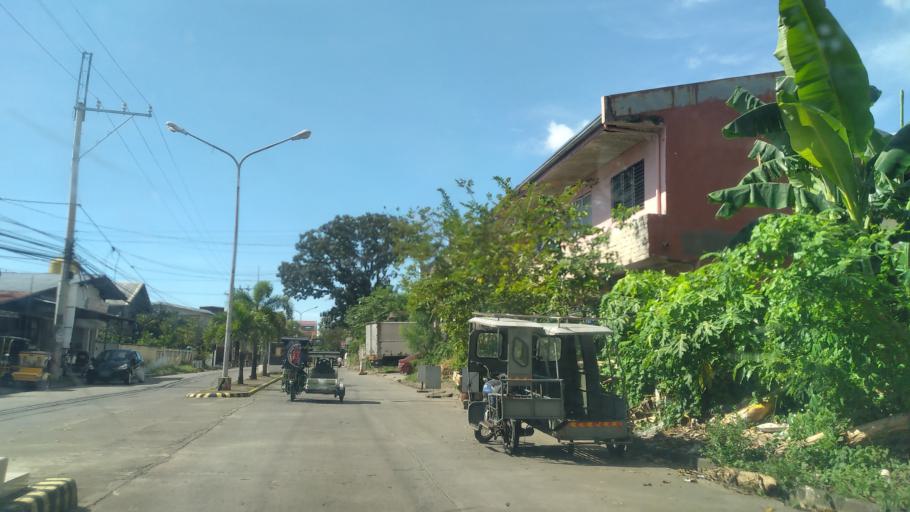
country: PH
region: Calabarzon
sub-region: Province of Quezon
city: Lucena
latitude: 13.9384
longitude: 121.6012
